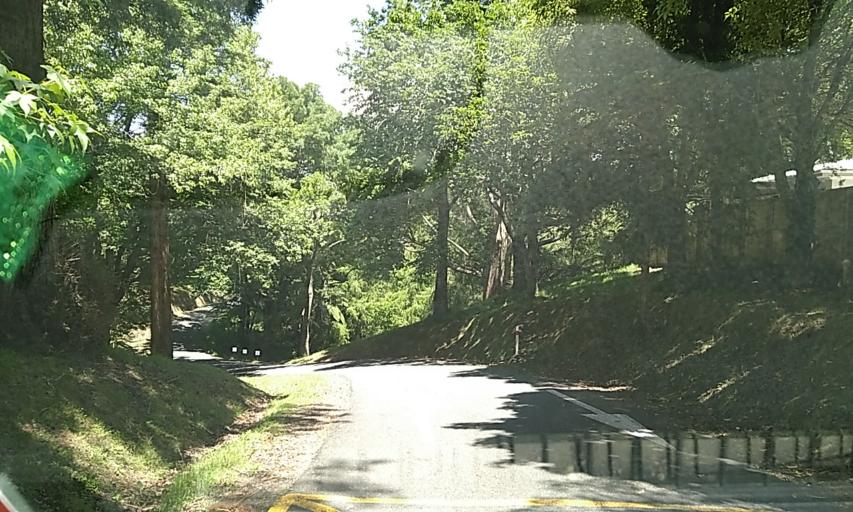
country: NZ
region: Bay of Plenty
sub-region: Tauranga City
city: Tauranga
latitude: -37.8098
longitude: 176.0448
